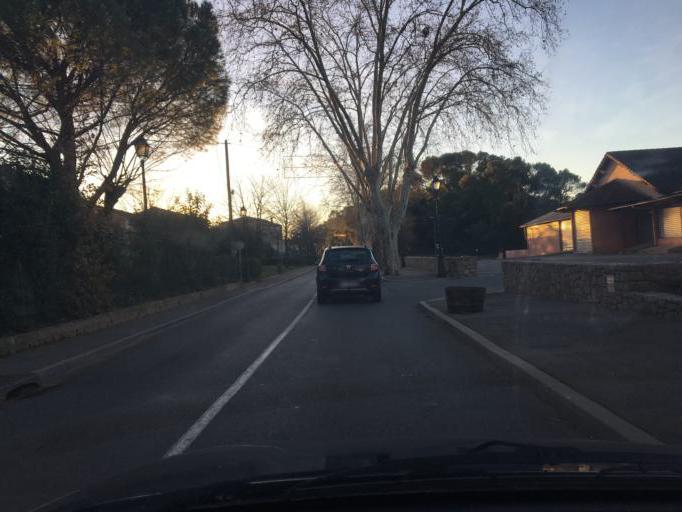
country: FR
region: Provence-Alpes-Cote d'Azur
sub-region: Departement du Var
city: Taradeau
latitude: 43.4532
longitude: 6.4283
